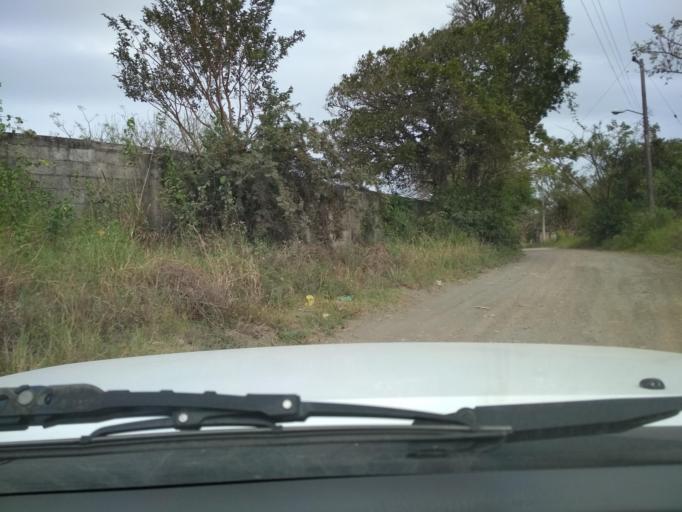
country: MX
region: Veracruz
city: El Tejar
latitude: 19.0659
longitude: -96.1371
